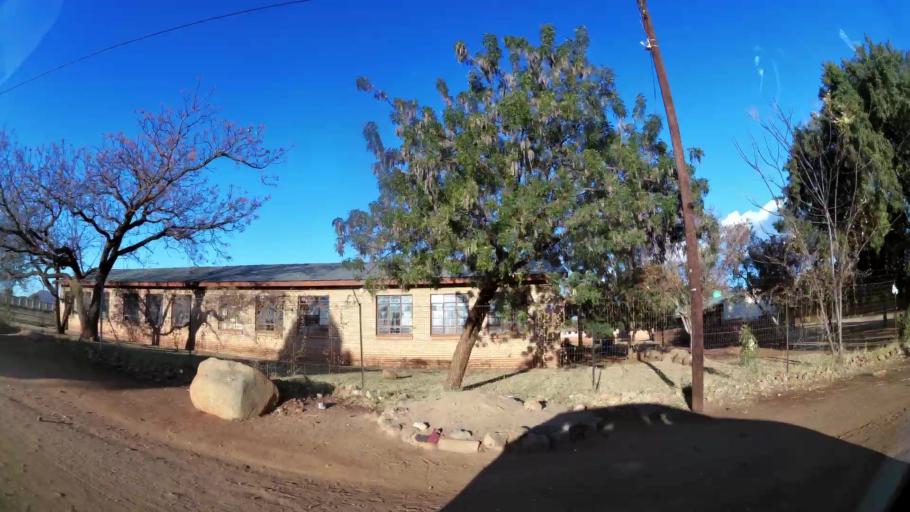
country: ZA
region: Limpopo
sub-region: Waterberg District Municipality
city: Mokopane
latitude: -24.1461
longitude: 28.9856
